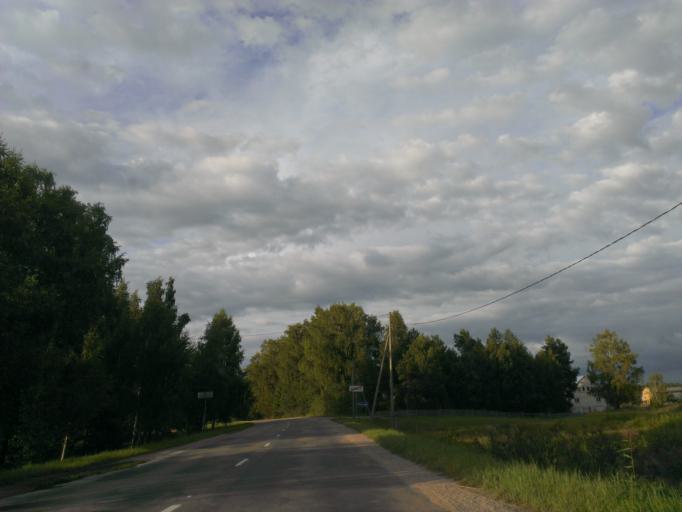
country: LV
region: Ikskile
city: Ikskile
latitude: 56.8462
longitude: 24.5035
